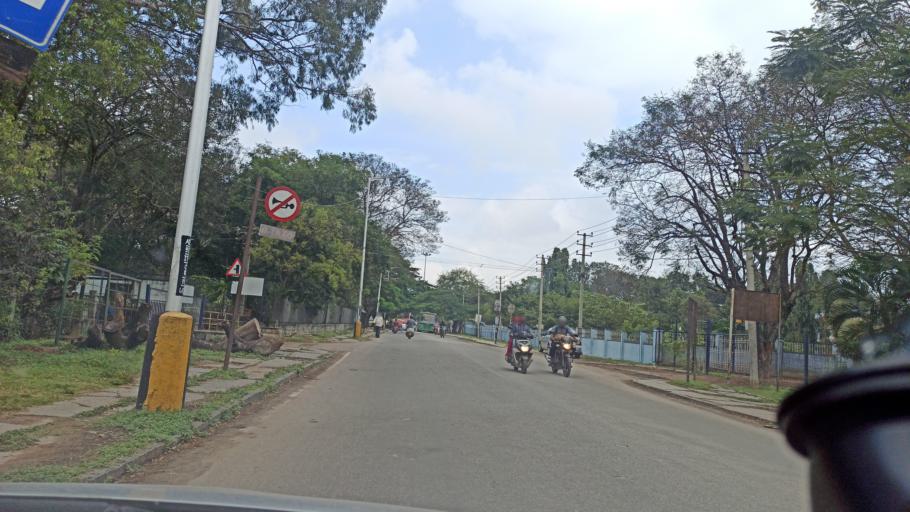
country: IN
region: Karnataka
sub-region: Bangalore Urban
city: Bangalore
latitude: 13.0062
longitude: 77.6843
